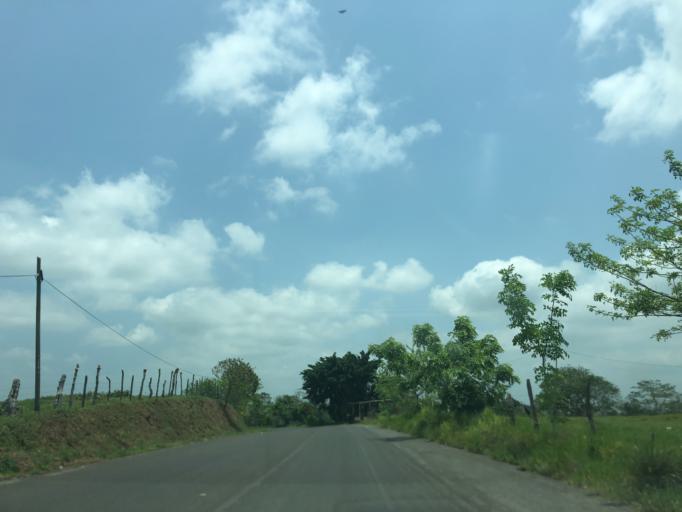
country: MX
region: Chiapas
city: Pueblo Juarez
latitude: 17.6020
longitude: -93.1820
